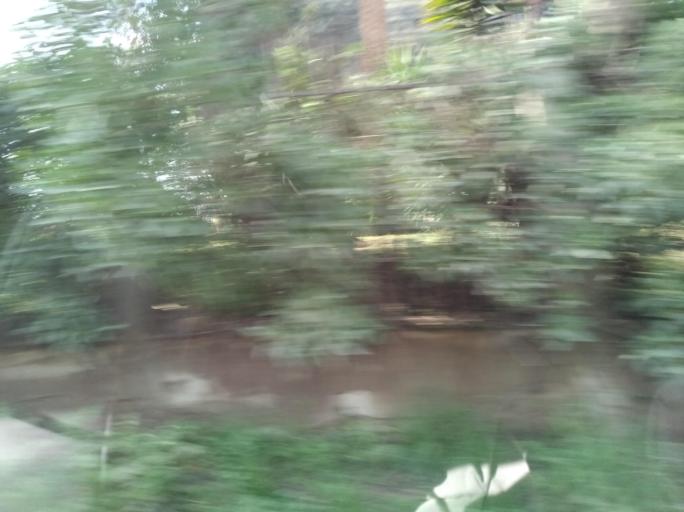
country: CL
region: Valparaiso
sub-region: Provincia de Marga Marga
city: Limache
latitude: -32.9970
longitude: -71.2340
